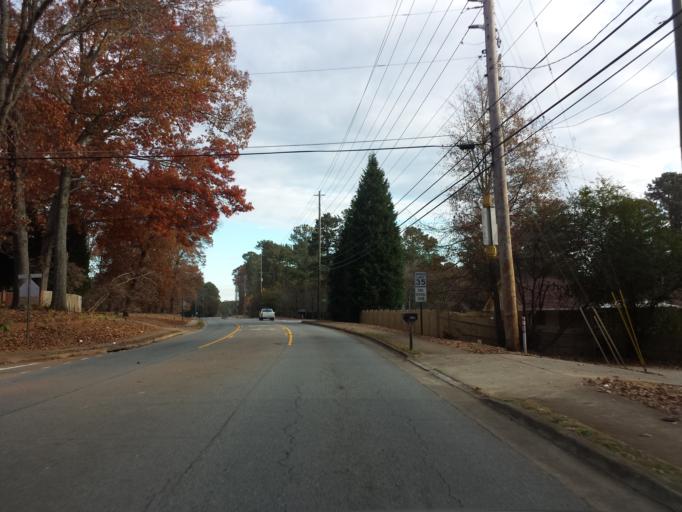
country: US
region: Georgia
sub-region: Cobb County
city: Fair Oaks
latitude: 33.9413
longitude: -84.4939
